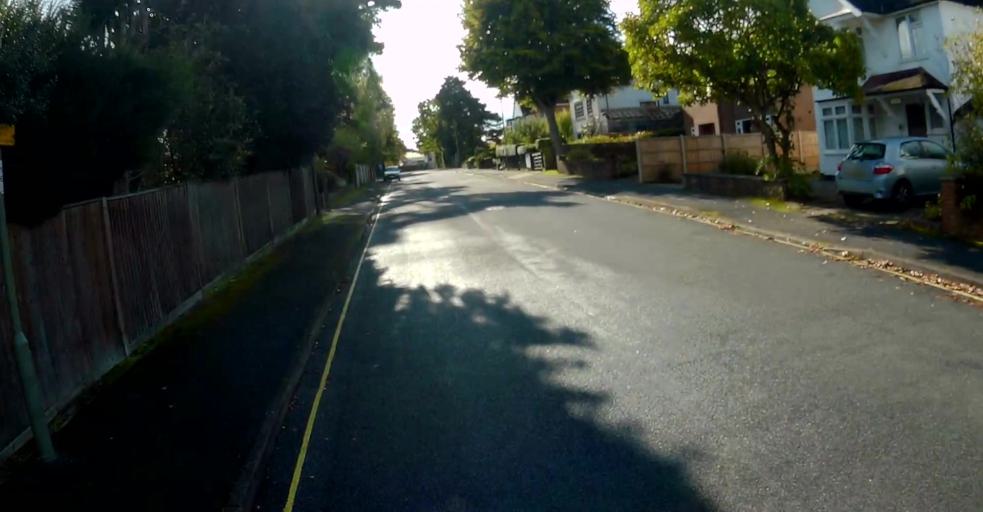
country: GB
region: England
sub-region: Hampshire
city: Farnborough
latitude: 51.2884
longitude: -0.7510
